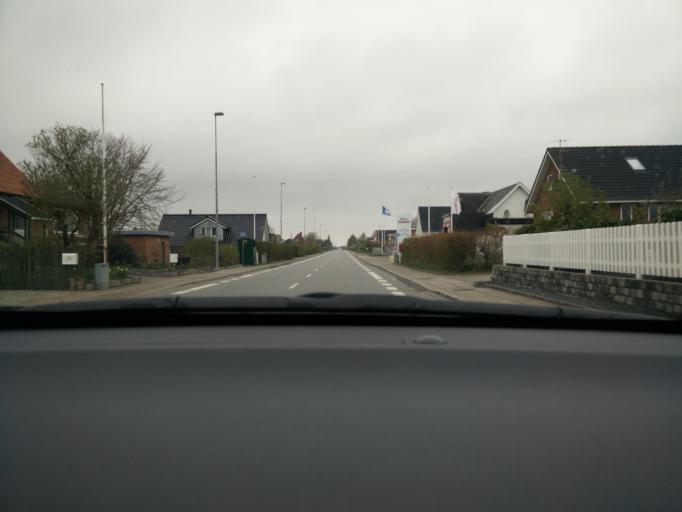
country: DK
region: Central Jutland
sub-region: Skive Kommune
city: Hojslev
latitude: 56.5448
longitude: 9.1258
